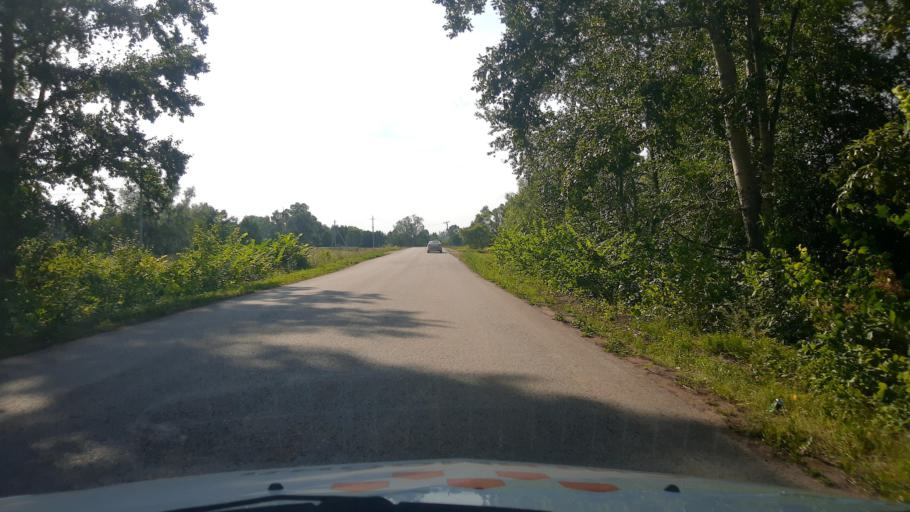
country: RU
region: Bashkortostan
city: Kabakovo
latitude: 54.6625
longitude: 56.1811
